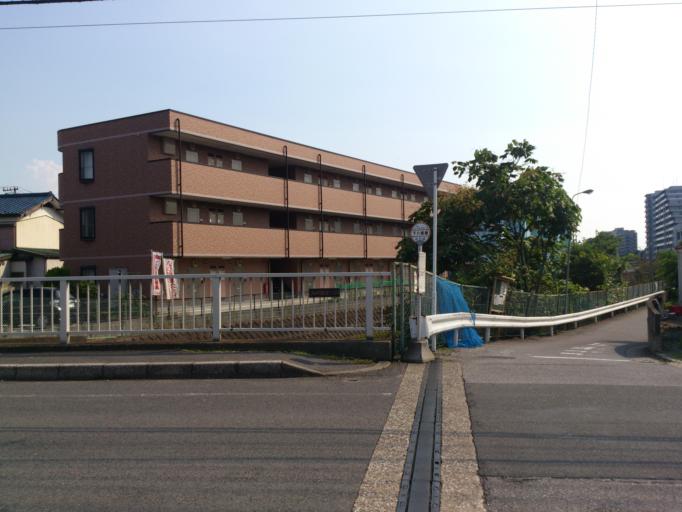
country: JP
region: Chiba
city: Funabashi
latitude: 35.6623
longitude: 140.0471
